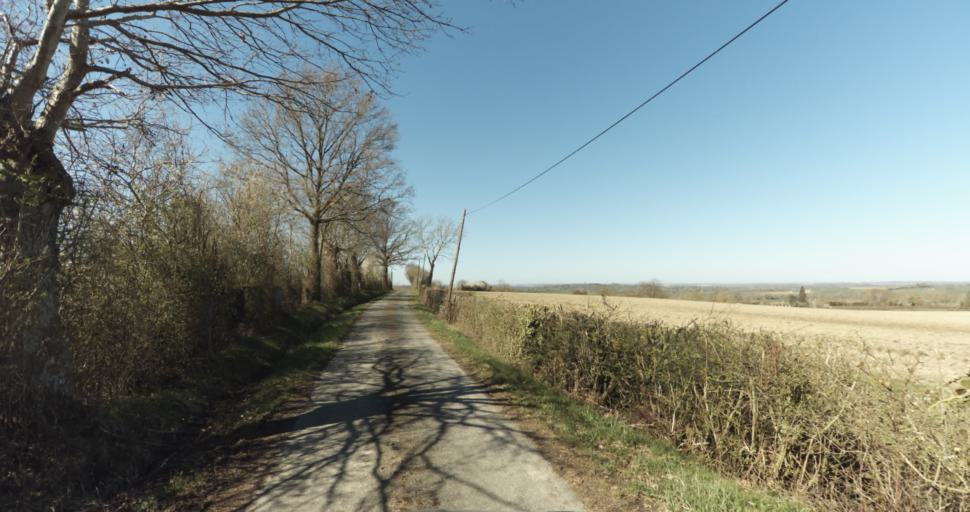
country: FR
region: Lower Normandy
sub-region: Departement de l'Orne
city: Trun
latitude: 48.9482
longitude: 0.0524
